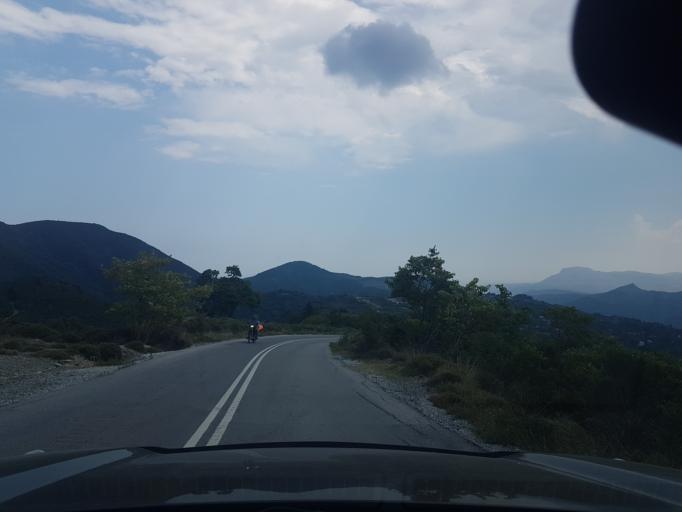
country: GR
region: Central Greece
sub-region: Nomos Evvoias
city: Kymi
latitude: 38.6451
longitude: 24.0574
